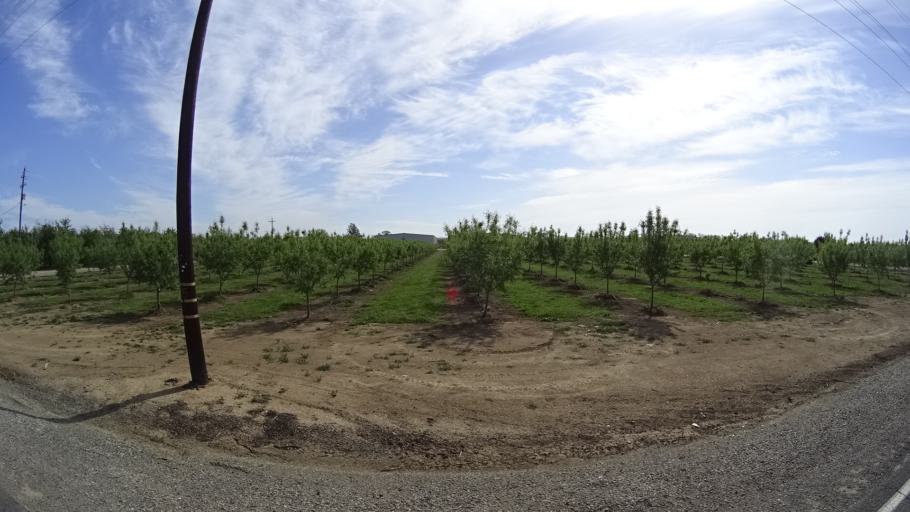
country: US
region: California
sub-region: Glenn County
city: Hamilton City
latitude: 39.6402
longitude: -122.0074
